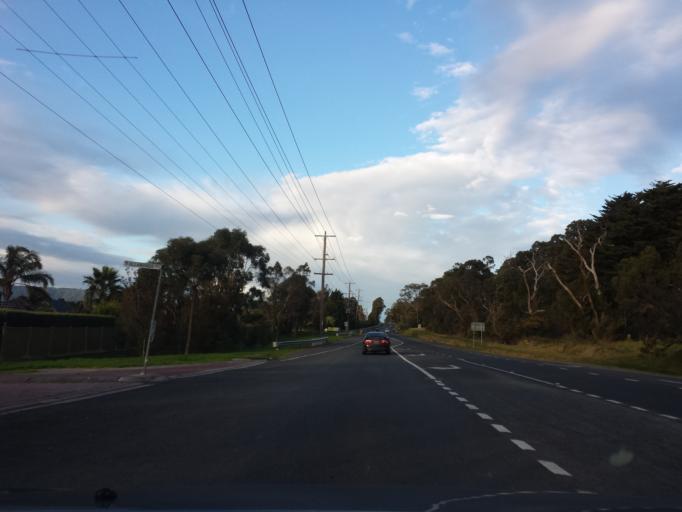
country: AU
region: Victoria
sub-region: Yarra Ranges
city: Lysterfield
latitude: -37.9281
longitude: 145.2737
